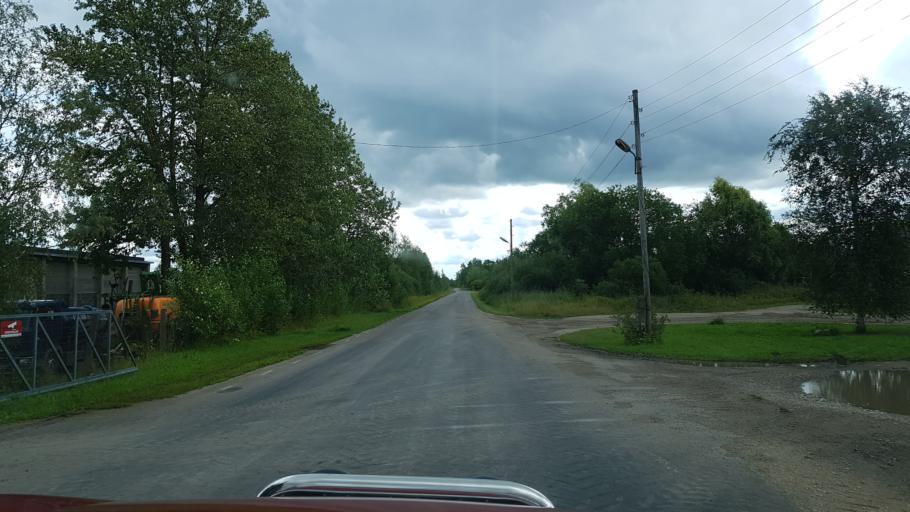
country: EE
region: Laeaene
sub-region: Lihula vald
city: Lihula
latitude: 58.7248
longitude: 23.9542
